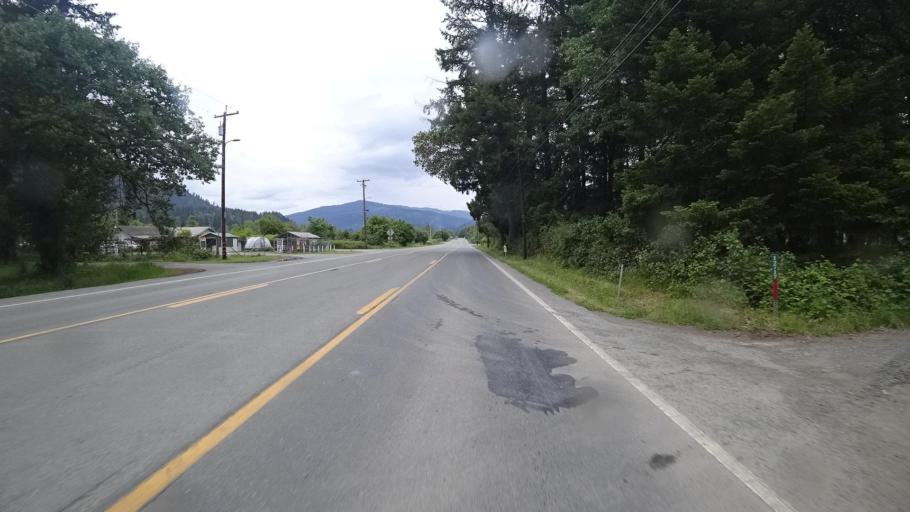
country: US
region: California
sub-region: Humboldt County
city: Willow Creek
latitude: 41.0664
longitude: -123.6863
